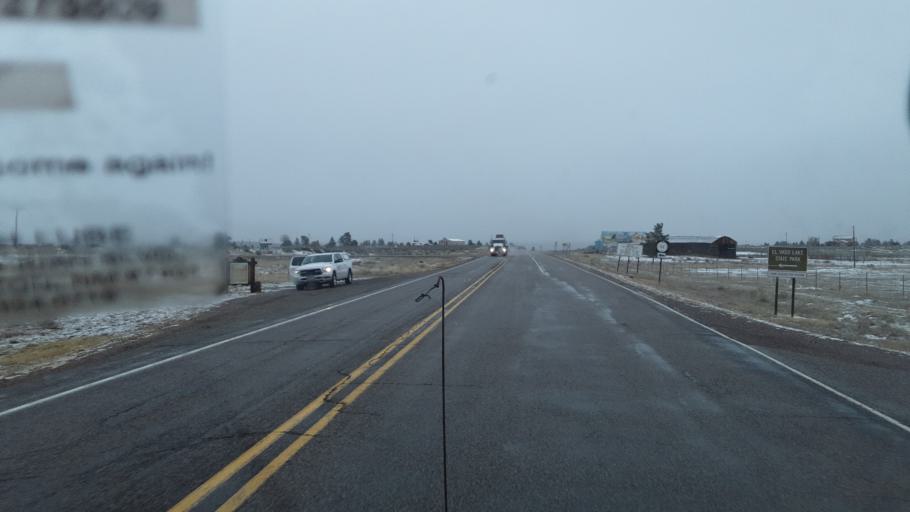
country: US
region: New Mexico
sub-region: Rio Arriba County
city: Tierra Amarilla
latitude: 36.7203
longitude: -106.5634
